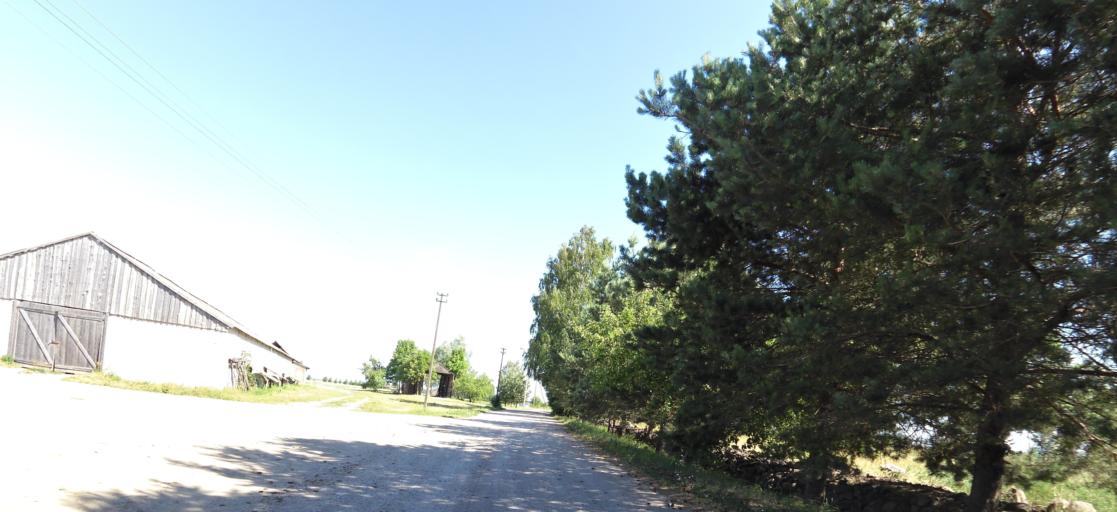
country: LT
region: Panevezys
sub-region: Birzai
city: Birzai
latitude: 56.2448
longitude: 24.8773
